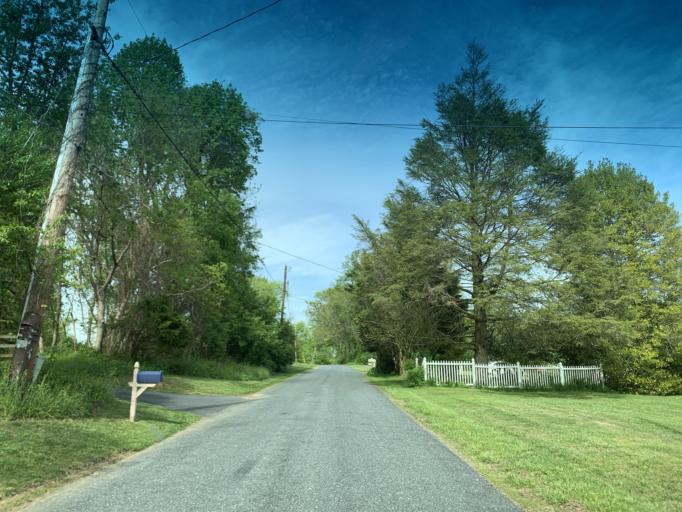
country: US
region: Maryland
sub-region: Harford County
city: South Bel Air
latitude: 39.6224
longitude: -76.2806
